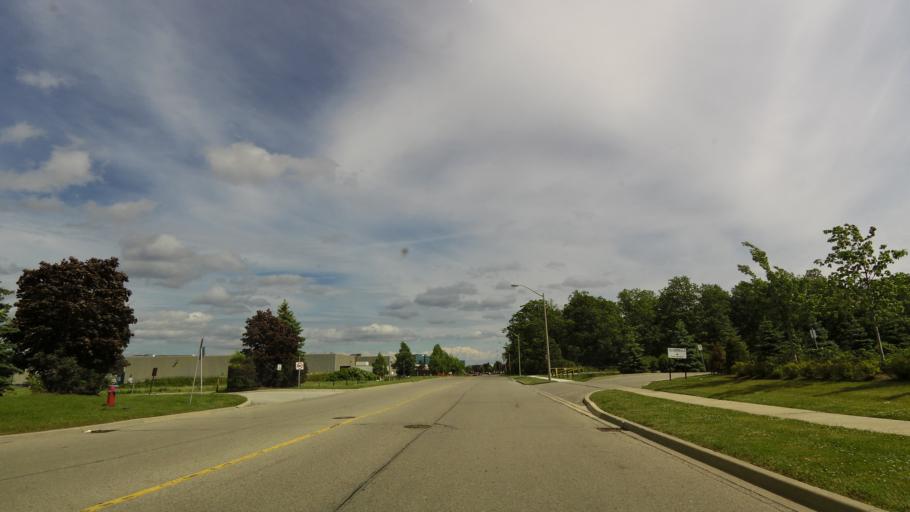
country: CA
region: Ontario
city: Oakville
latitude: 43.5122
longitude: -79.6780
